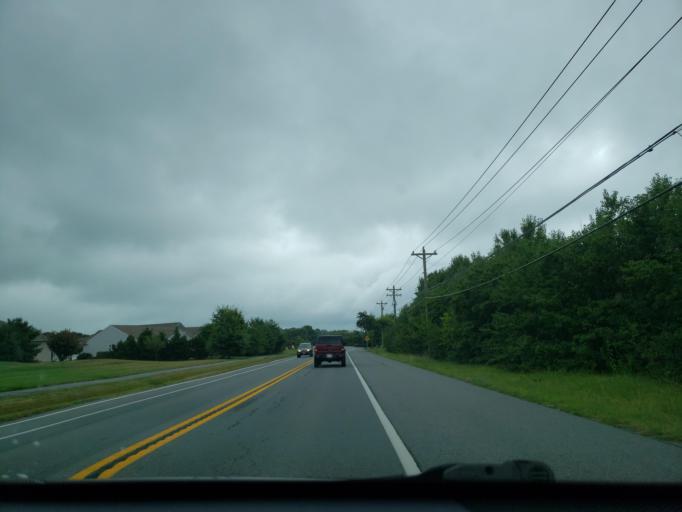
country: US
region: Delaware
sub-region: Sussex County
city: Milton
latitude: 38.7577
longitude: -75.2312
